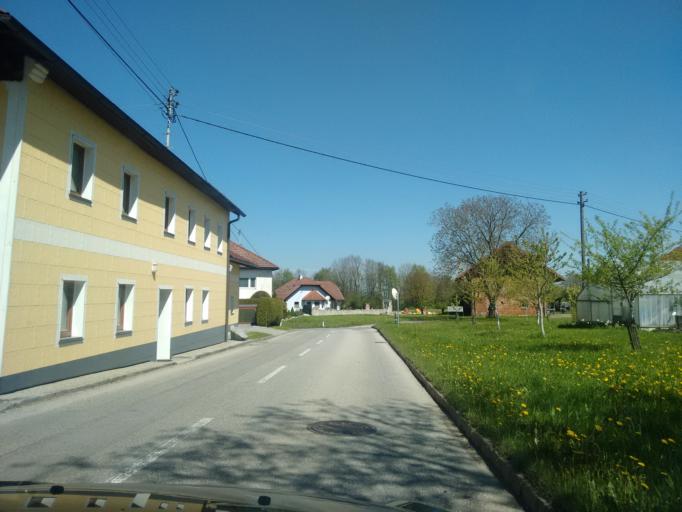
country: AT
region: Upper Austria
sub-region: Politischer Bezirk Vocklabruck
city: Wolfsegg am Hausruck
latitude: 48.2001
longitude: 13.6044
